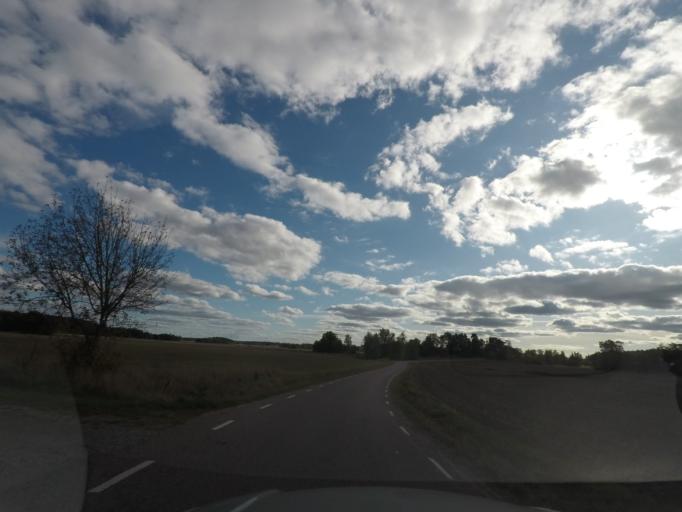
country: SE
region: Vaestmanland
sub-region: Hallstahammars Kommun
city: Kolback
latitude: 59.5197
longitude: 16.1898
